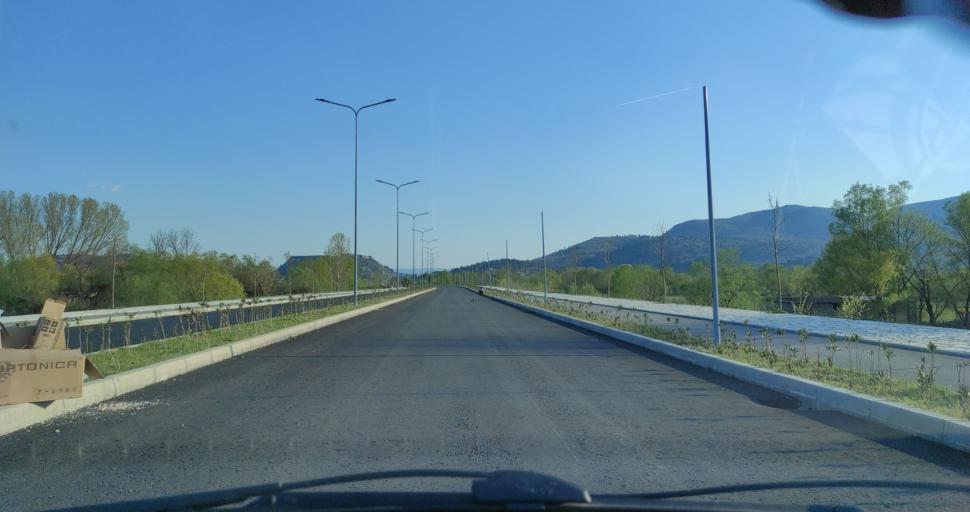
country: AL
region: Shkoder
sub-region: Rrethi i Shkodres
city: Shkoder
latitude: 42.0705
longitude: 19.4893
